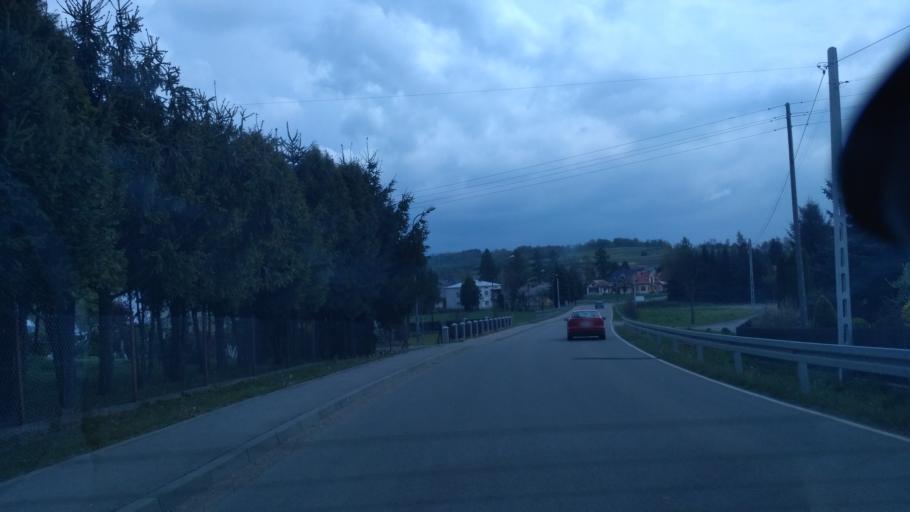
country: PL
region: Subcarpathian Voivodeship
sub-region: Powiat brzozowski
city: Haczow
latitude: 49.6655
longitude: 21.9008
